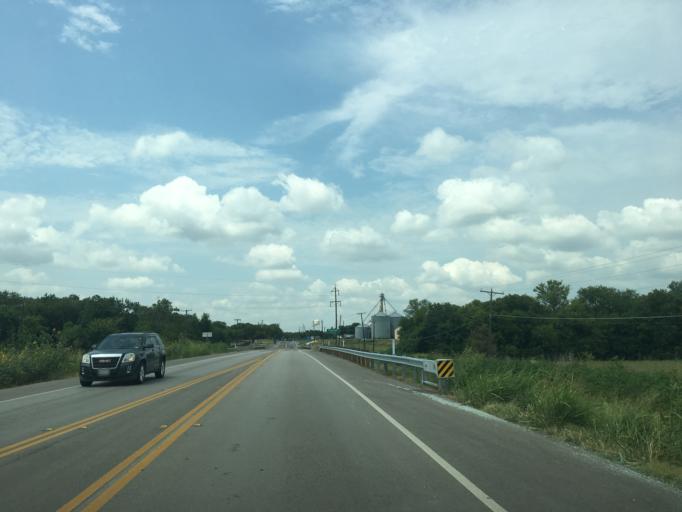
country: US
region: Texas
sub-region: Rockwall County
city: Royse City
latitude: 32.9828
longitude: -96.3219
